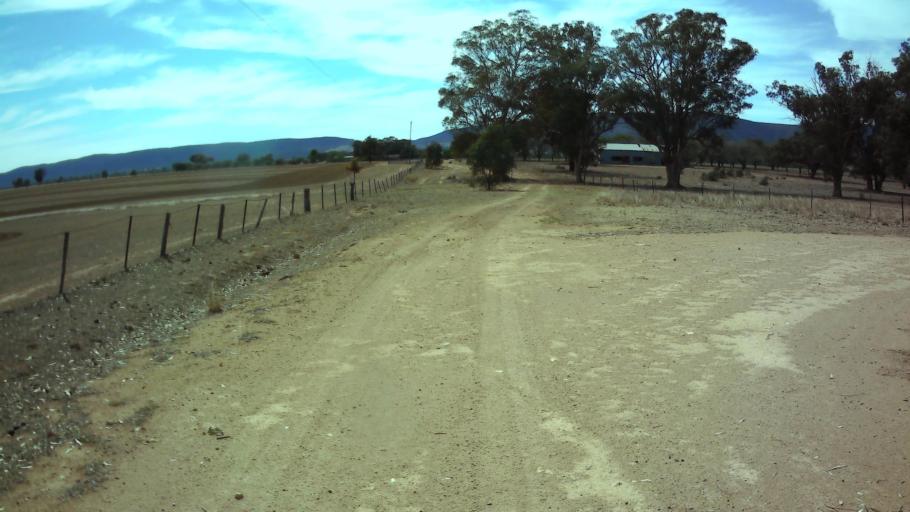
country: AU
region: New South Wales
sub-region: Weddin
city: Grenfell
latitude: -33.7218
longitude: 148.2677
